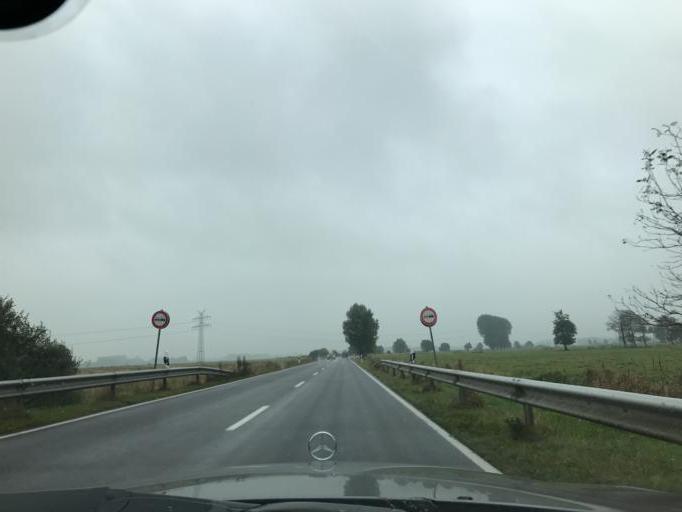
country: DE
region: Lower Saxony
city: Weener
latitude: 53.1230
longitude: 7.3342
